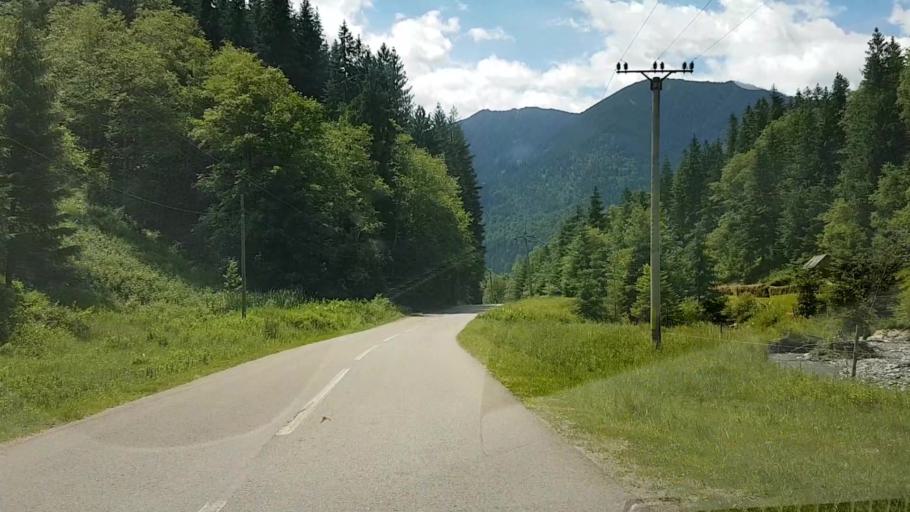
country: RO
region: Suceava
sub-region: Comuna Crucea
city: Crucea
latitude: 47.4092
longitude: 25.5788
